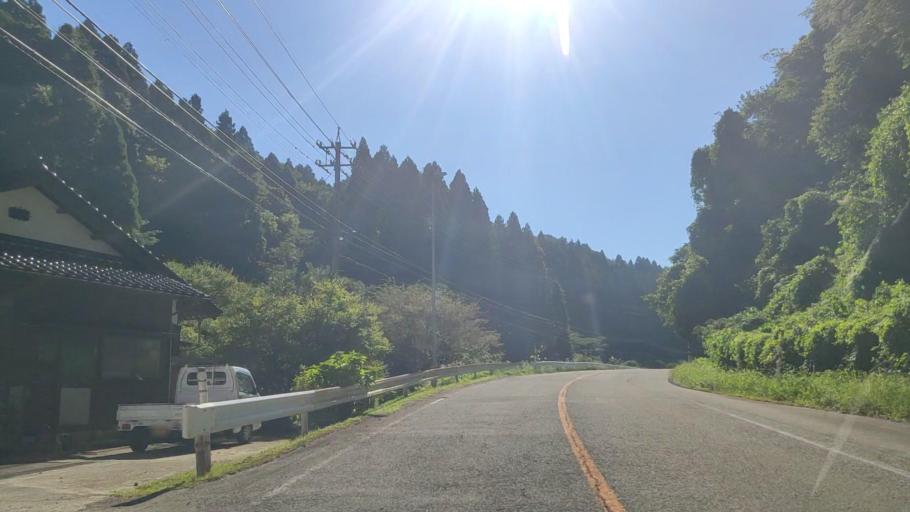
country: JP
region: Ishikawa
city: Nanao
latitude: 37.3219
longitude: 137.1890
